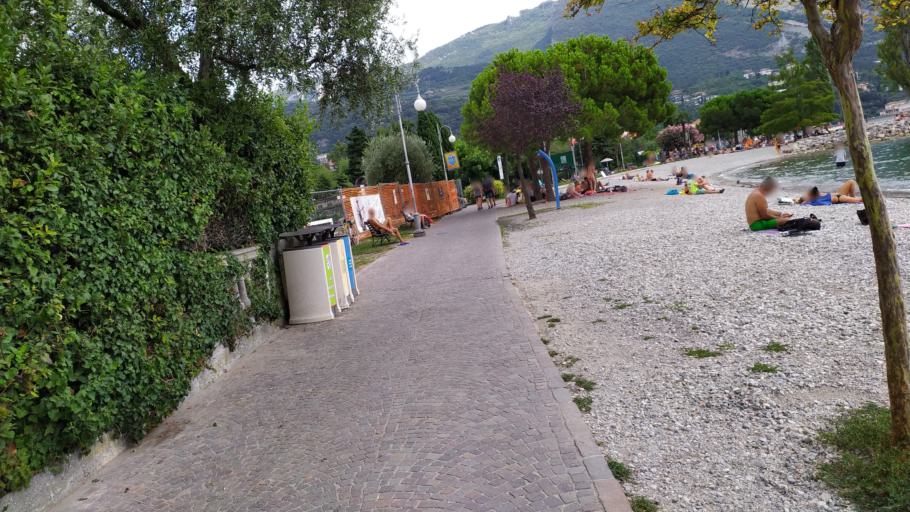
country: IT
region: Trentino-Alto Adige
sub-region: Provincia di Trento
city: Torbole sul Garda
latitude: 45.8723
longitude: 10.8693
